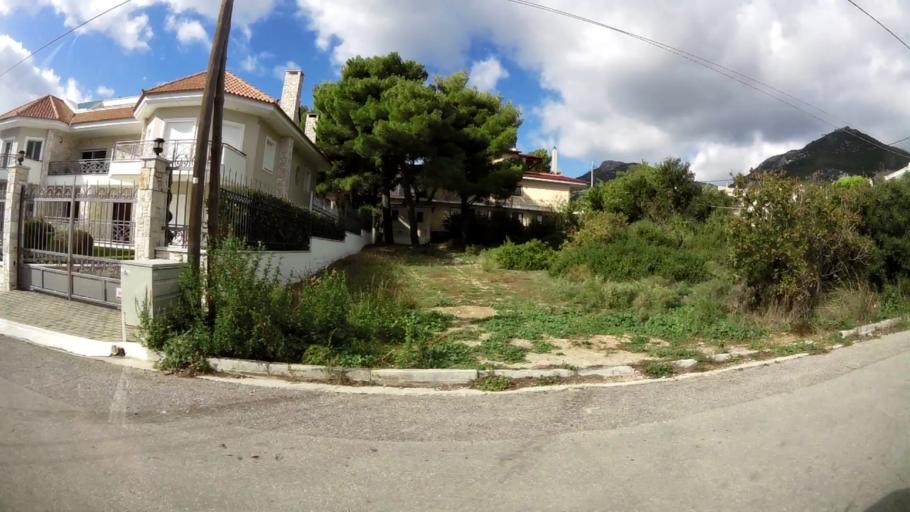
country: GR
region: Attica
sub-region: Nomarchia Anatolikis Attikis
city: Thrakomakedones
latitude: 38.1378
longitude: 23.7530
